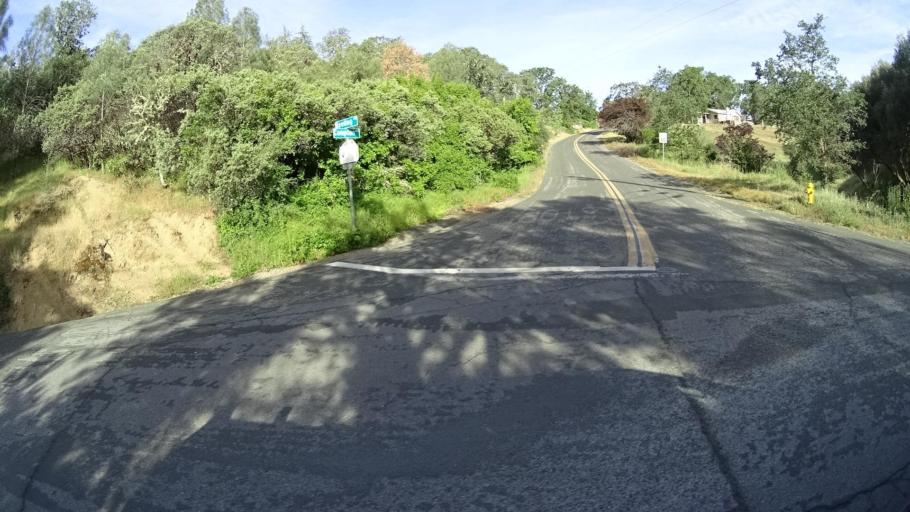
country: US
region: California
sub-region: Lake County
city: North Lakeport
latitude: 39.0735
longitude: -122.9201
